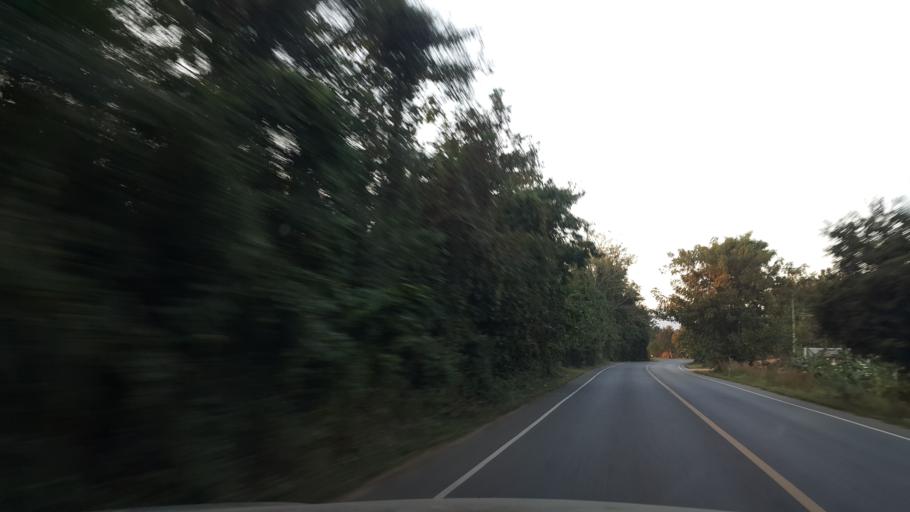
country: TH
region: Phrae
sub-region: Amphoe Wang Chin
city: Wang Chin
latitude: 17.8598
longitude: 99.6254
